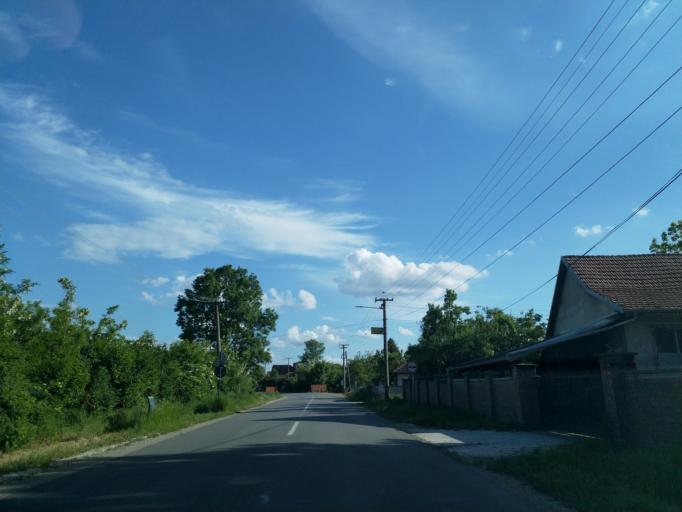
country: RS
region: Central Serbia
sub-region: Sumadijski Okrug
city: Lapovo
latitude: 44.1886
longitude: 21.0909
